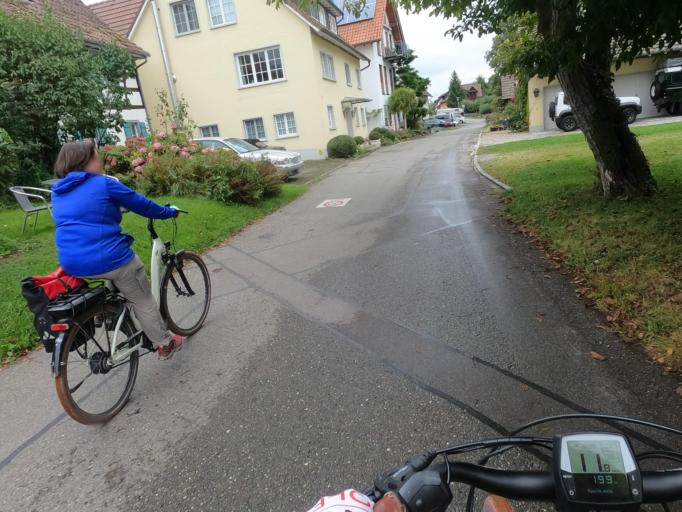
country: DE
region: Baden-Wuerttemberg
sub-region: Freiburg Region
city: Reichenau
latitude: 47.6929
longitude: 9.0779
